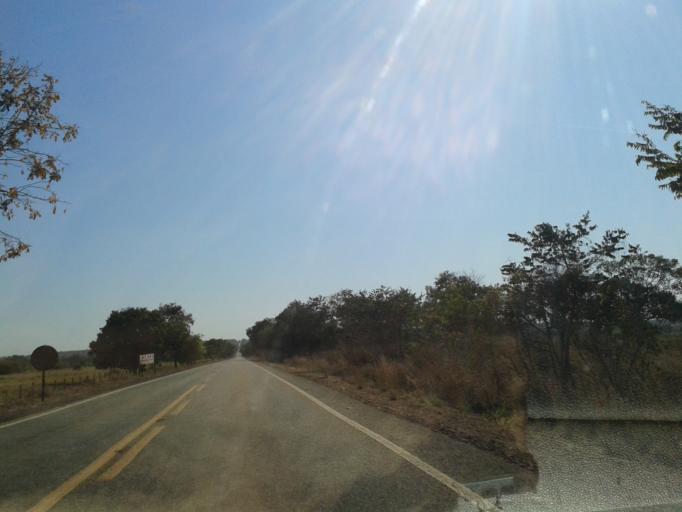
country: BR
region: Goias
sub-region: Mozarlandia
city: Mozarlandia
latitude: -14.5916
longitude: -50.5083
